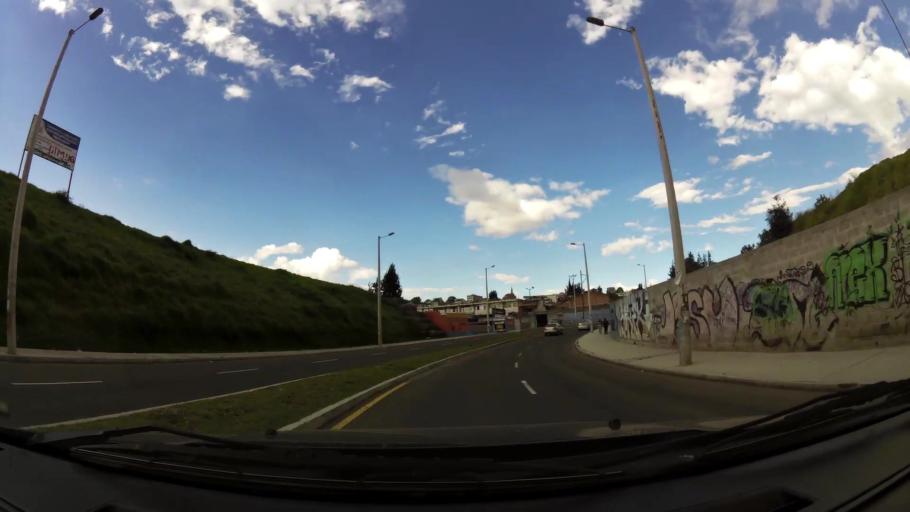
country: EC
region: Pichincha
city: Quito
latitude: -0.1261
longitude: -78.4906
